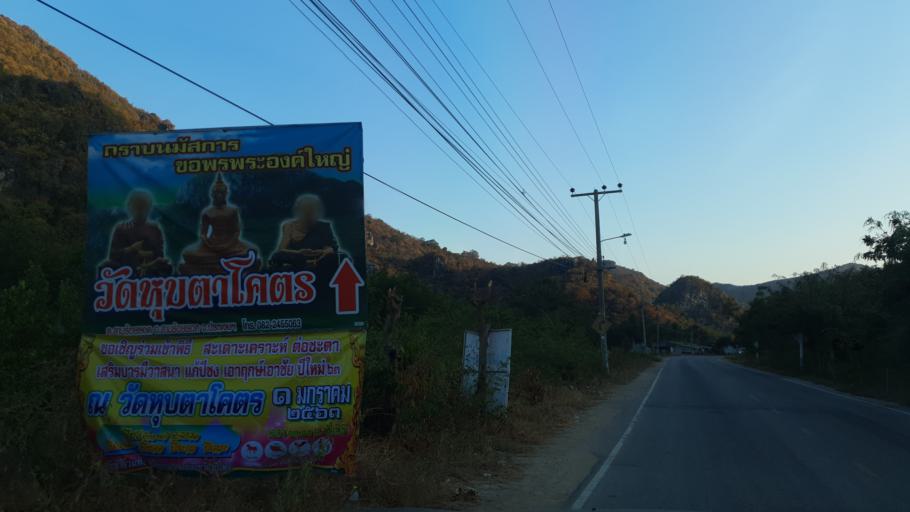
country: TH
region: Prachuap Khiri Khan
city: Sam Roi Yot
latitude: 12.2022
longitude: 100.0057
